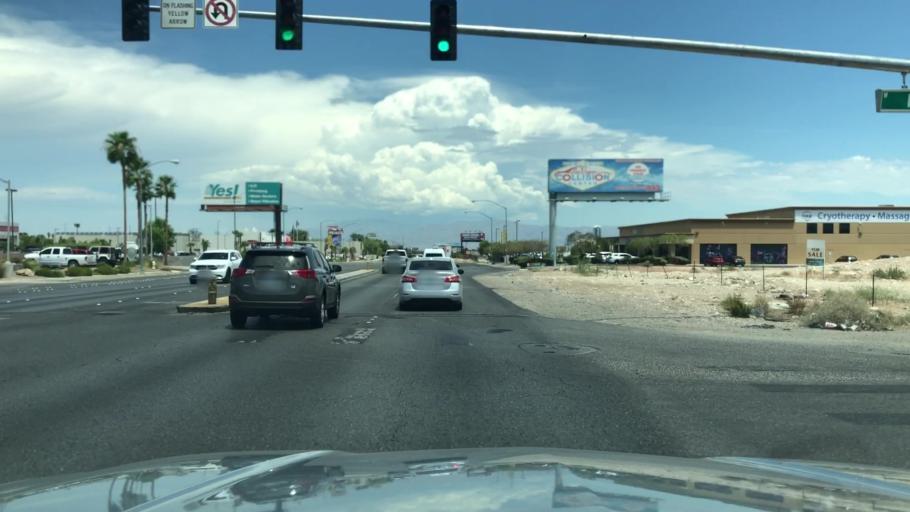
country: US
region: Nevada
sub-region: Clark County
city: Spring Valley
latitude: 36.0754
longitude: -115.2078
